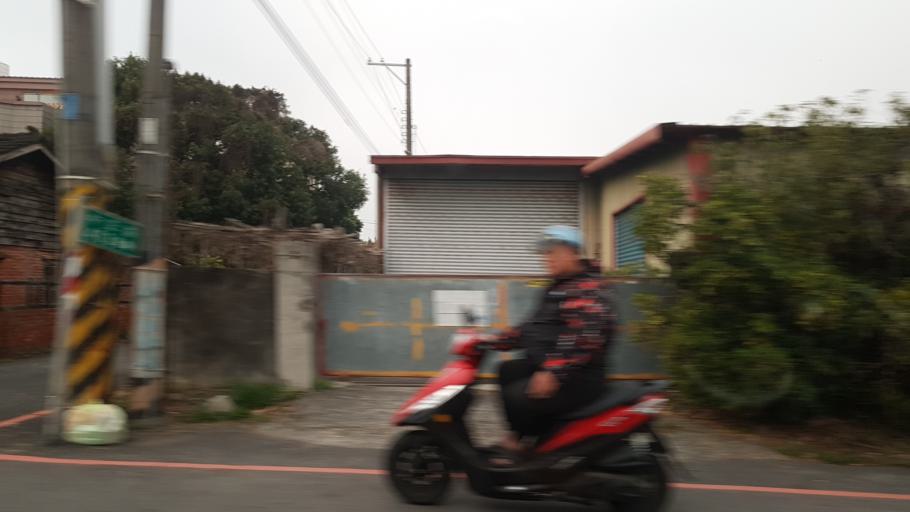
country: TW
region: Taiwan
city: Xinying
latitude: 23.3228
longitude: 120.3161
